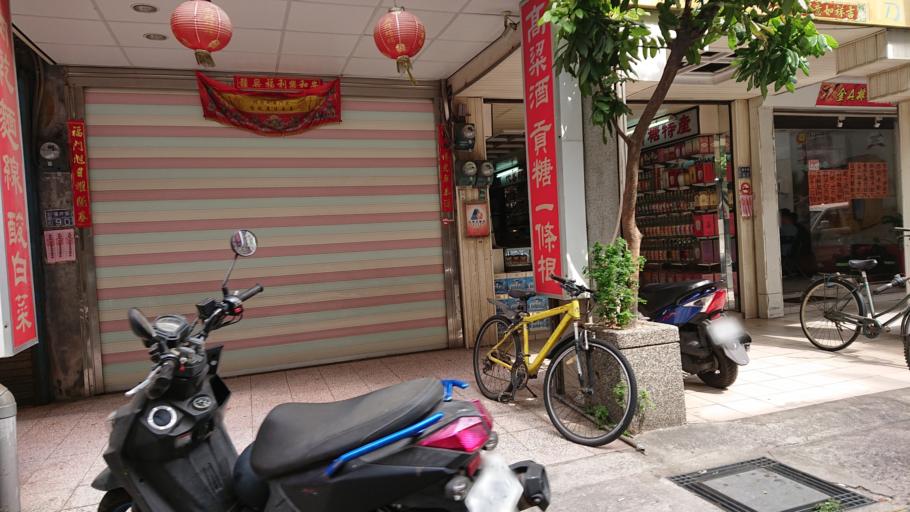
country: TW
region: Fukien
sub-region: Kinmen
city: Jincheng
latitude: 24.4418
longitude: 118.4152
